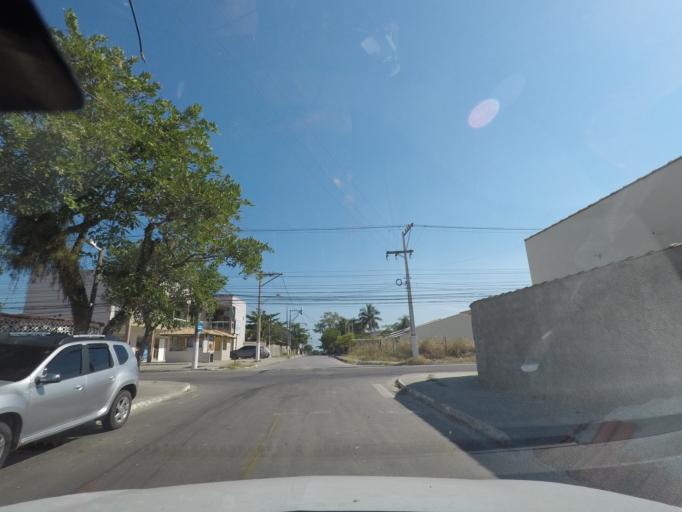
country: BR
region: Rio de Janeiro
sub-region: Niteroi
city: Niteroi
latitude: -22.9645
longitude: -42.9738
